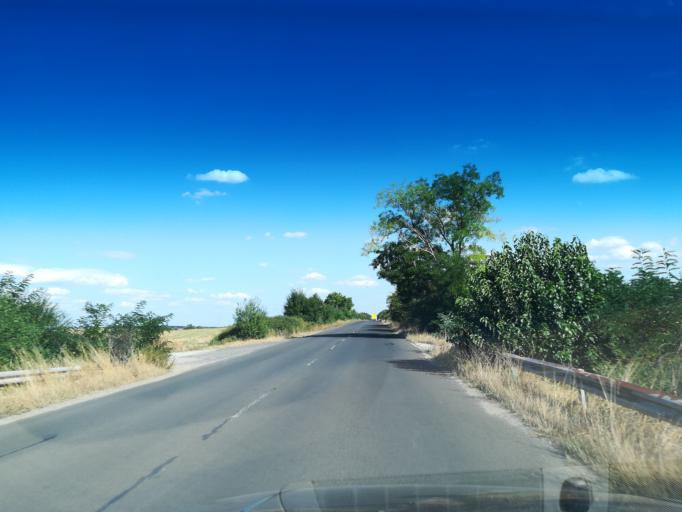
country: BG
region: Stara Zagora
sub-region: Obshtina Chirpan
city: Chirpan
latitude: 42.0700
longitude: 25.2142
